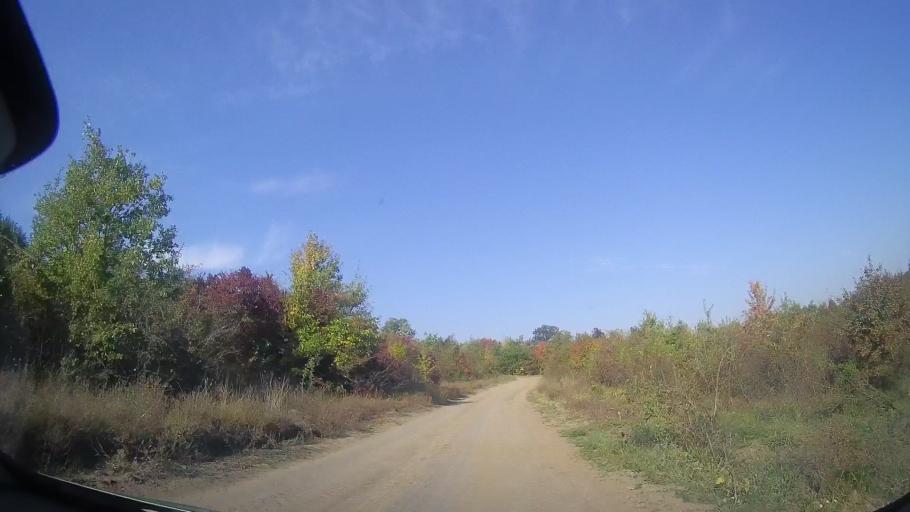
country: RO
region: Timis
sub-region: Comuna Bogda
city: Bogda
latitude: 45.9091
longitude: 21.5862
